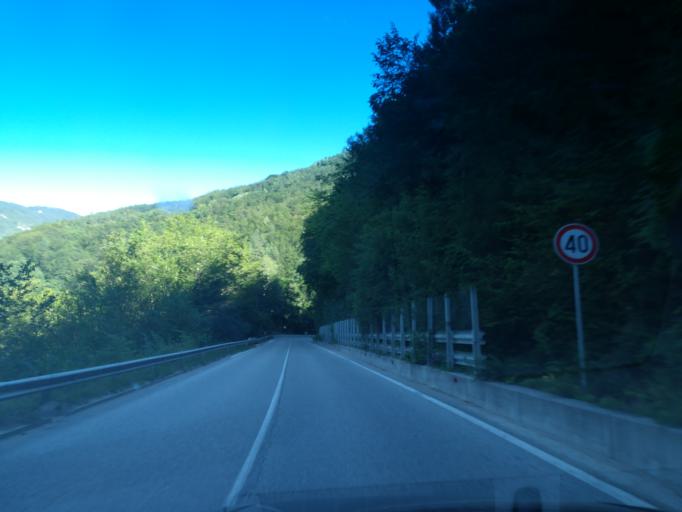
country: BG
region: Smolyan
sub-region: Obshtina Chepelare
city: Chepelare
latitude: 41.8045
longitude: 24.7091
